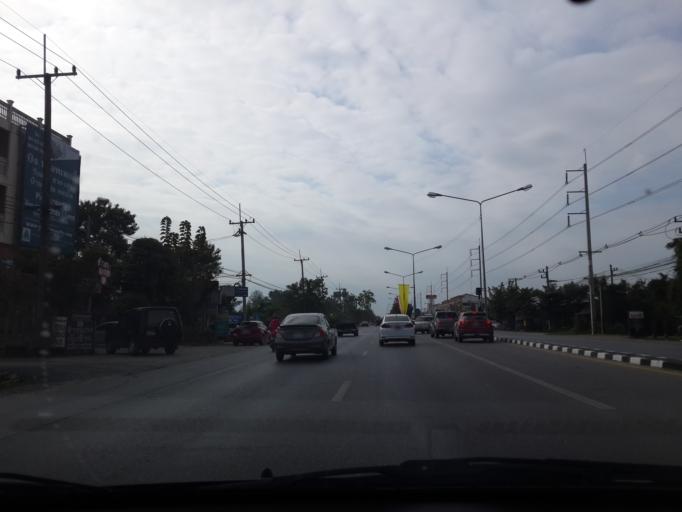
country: TH
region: Chiang Mai
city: San Sai
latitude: 18.8652
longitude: 99.0151
